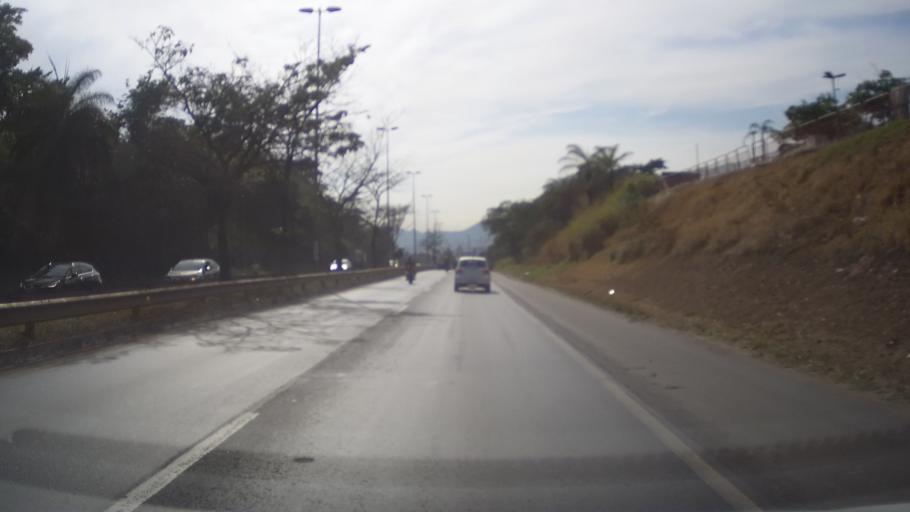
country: BR
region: Minas Gerais
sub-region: Contagem
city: Contagem
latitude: -19.9228
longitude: -44.0205
